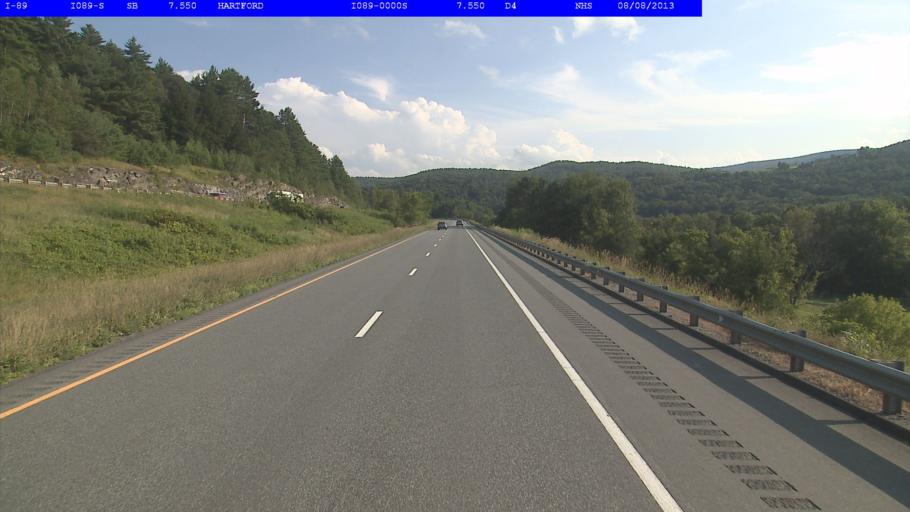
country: US
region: Vermont
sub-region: Windsor County
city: Wilder
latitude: 43.7134
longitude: -72.4136
